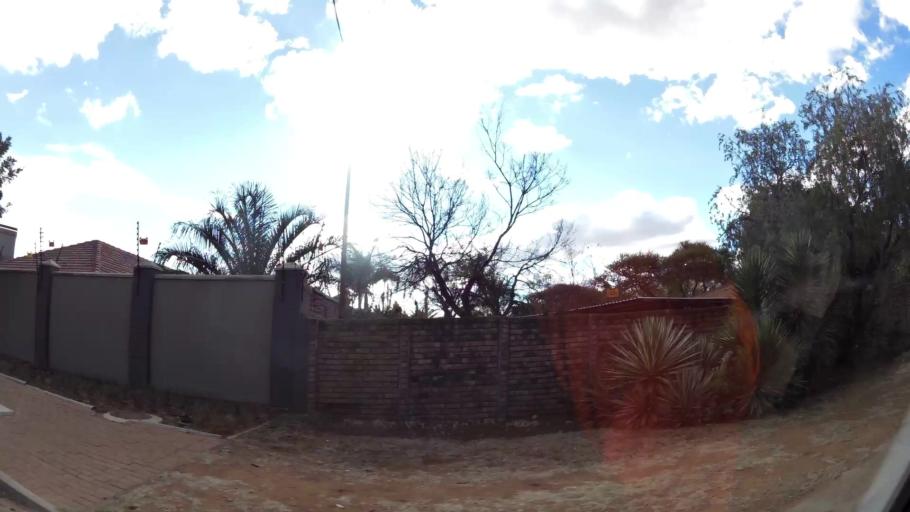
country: ZA
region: Limpopo
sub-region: Capricorn District Municipality
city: Polokwane
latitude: -23.8938
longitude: 29.4781
